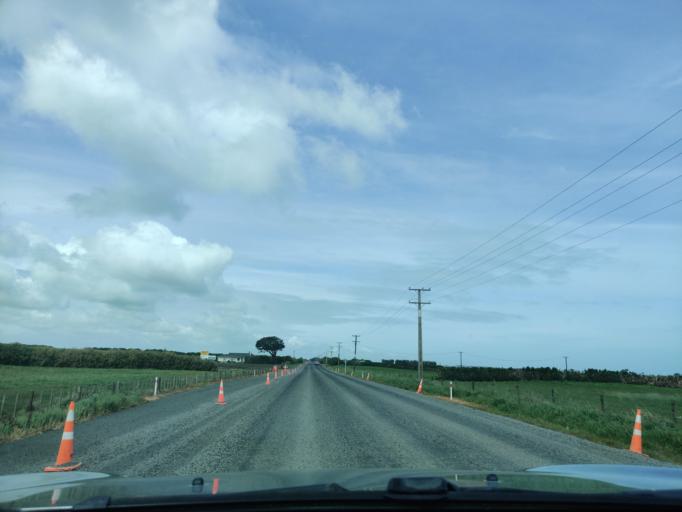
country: NZ
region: Taranaki
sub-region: South Taranaki District
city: Hawera
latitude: -39.5810
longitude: 174.2307
